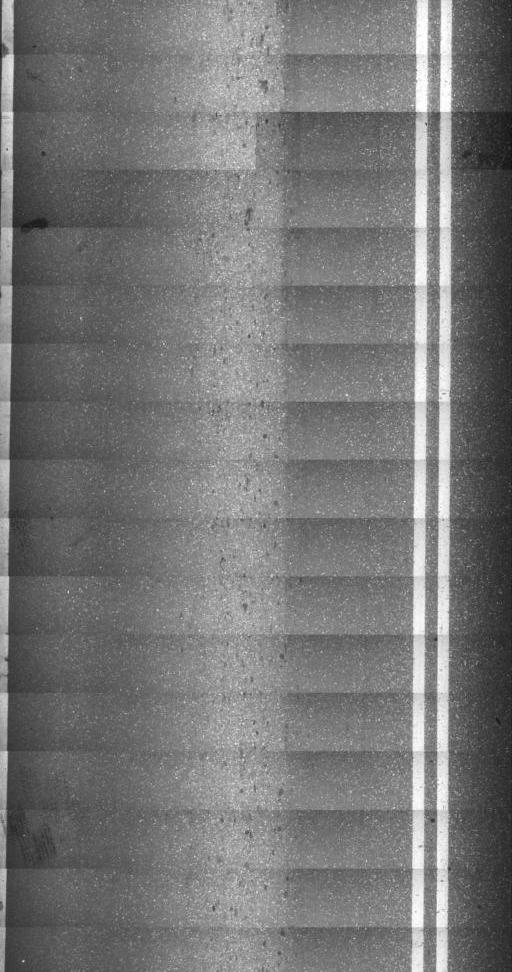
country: US
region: Vermont
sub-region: Orange County
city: Randolph
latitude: 43.9256
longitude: -72.6659
